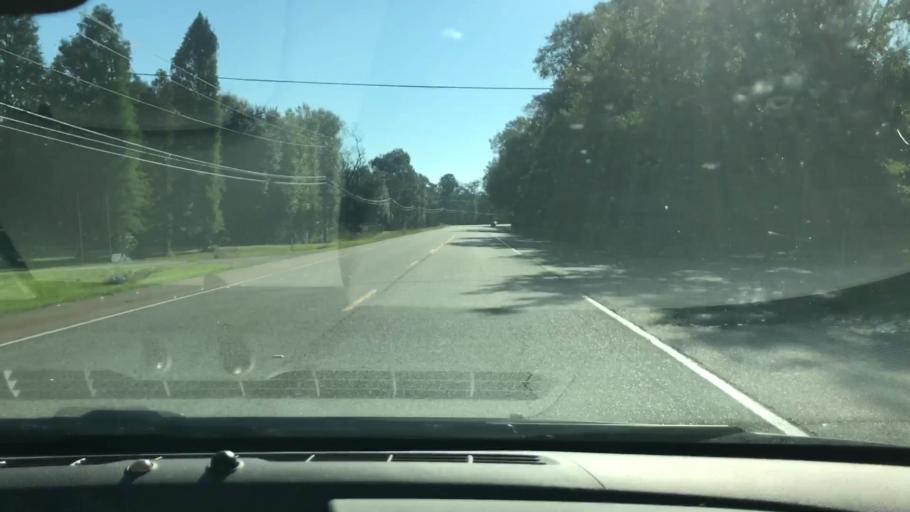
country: US
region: Louisiana
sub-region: Saint Tammany Parish
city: Pearl River
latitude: 30.4051
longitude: -89.7688
